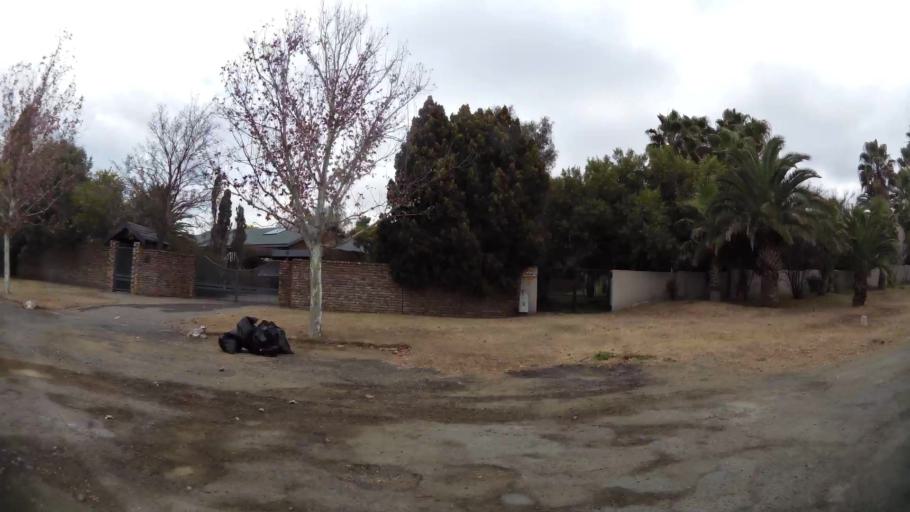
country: ZA
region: Orange Free State
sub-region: Fezile Dabi District Municipality
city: Kroonstad
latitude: -27.6852
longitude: 27.2395
